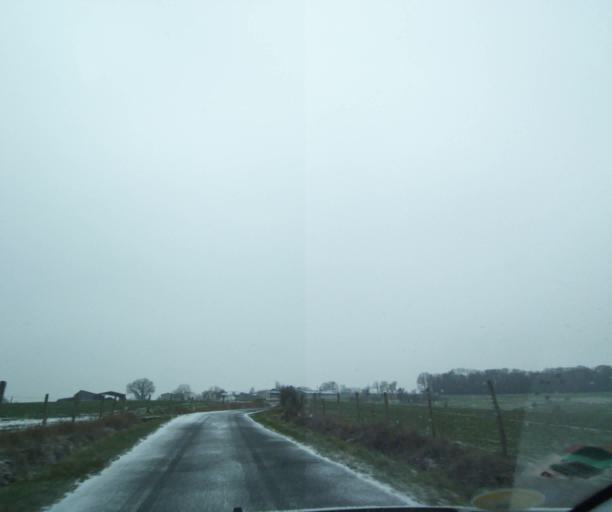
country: FR
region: Champagne-Ardenne
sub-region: Departement de la Haute-Marne
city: Wassy
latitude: 48.4790
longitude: 5.0401
